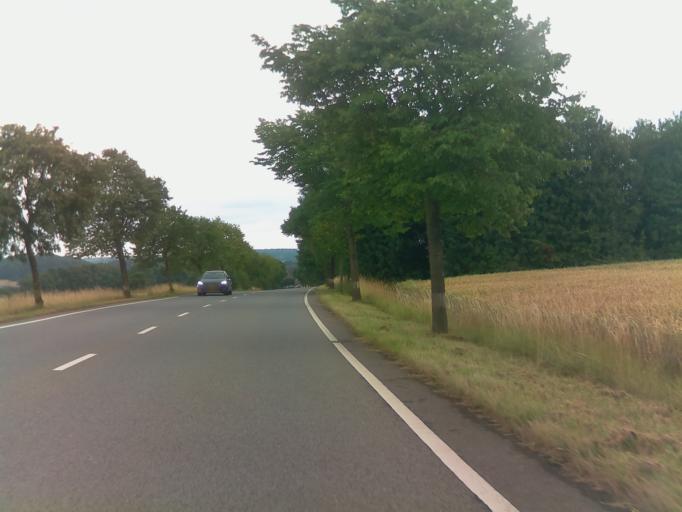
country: LU
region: Luxembourg
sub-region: Canton de Capellen
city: Dippach
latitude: 49.5806
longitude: 5.9840
